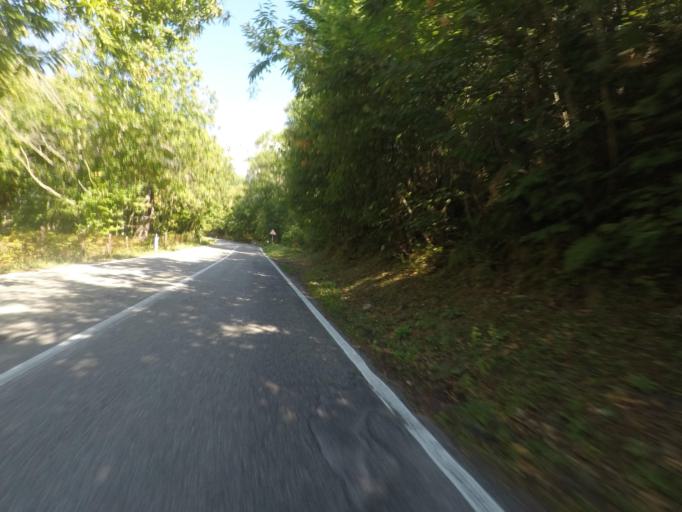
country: IT
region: Tuscany
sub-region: Provincia di Massa-Carrara
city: Fivizzano
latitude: 44.2421
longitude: 10.1448
